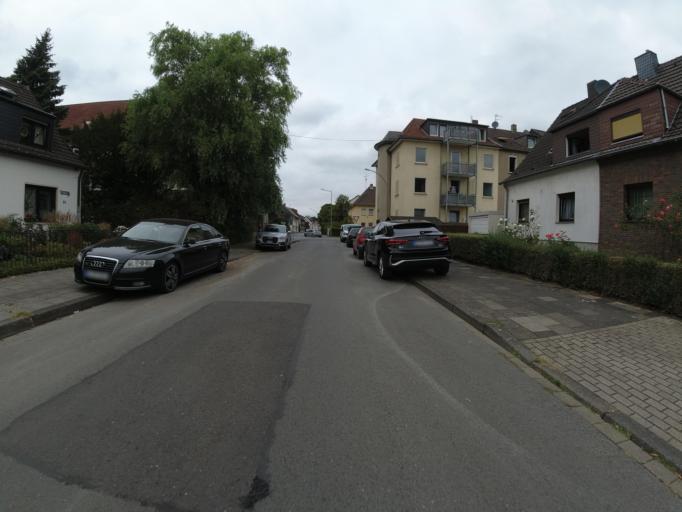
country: DE
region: North Rhine-Westphalia
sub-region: Regierungsbezirk Dusseldorf
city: Moers
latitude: 51.4539
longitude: 6.6904
